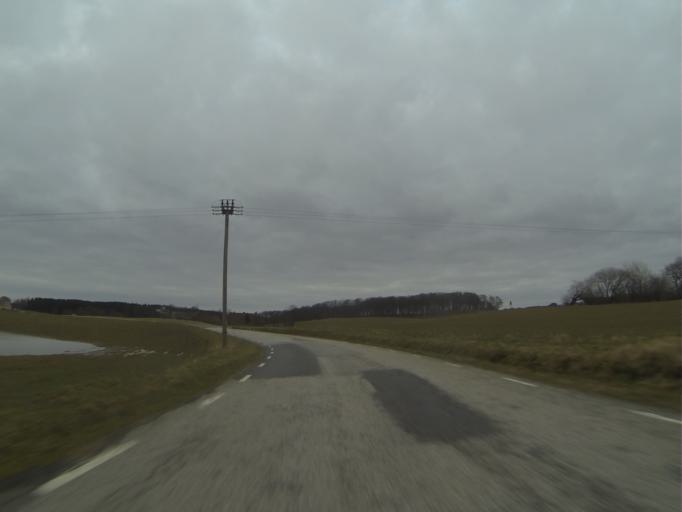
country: SE
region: Skane
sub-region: Skurups Kommun
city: Skurup
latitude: 55.5242
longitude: 13.4425
